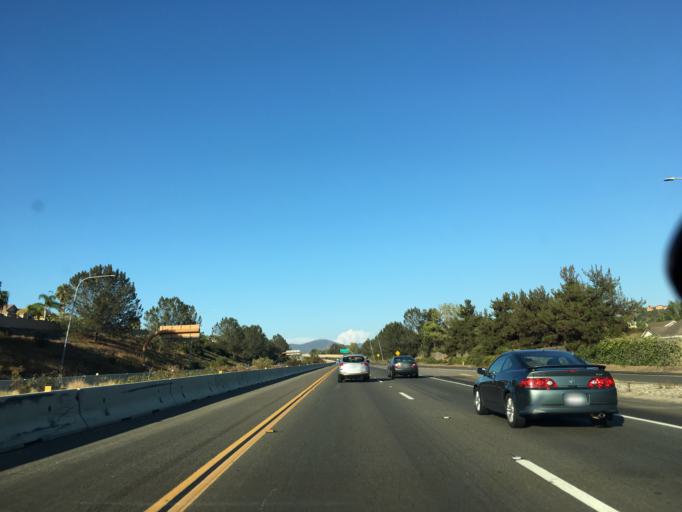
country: US
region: California
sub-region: San Diego County
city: Fairbanks Ranch
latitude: 32.9451
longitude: -117.2118
